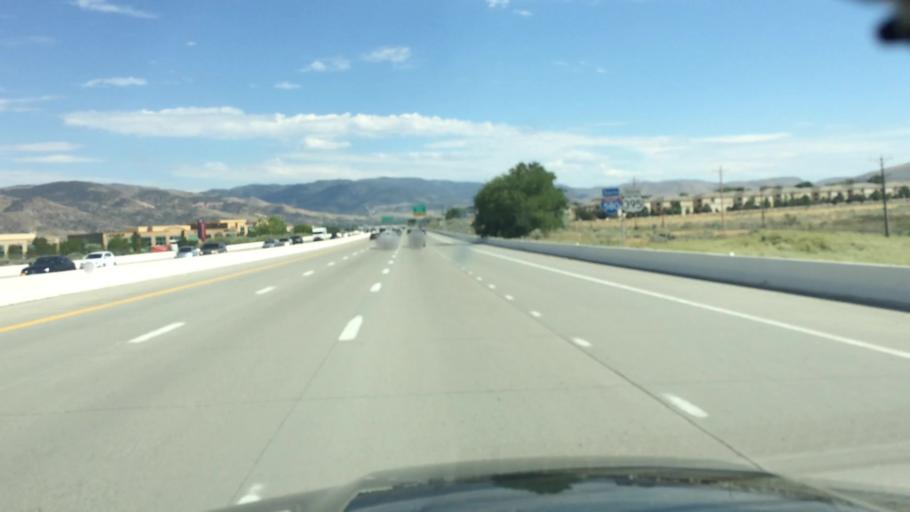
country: US
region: Nevada
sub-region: Washoe County
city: Sparks
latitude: 39.4349
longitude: -119.7625
